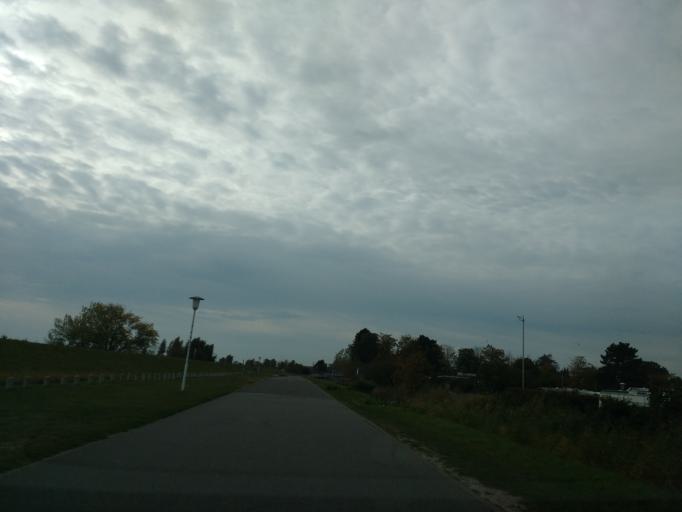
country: DE
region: Schleswig-Holstein
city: Gromitz
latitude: 54.1616
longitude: 11.0048
